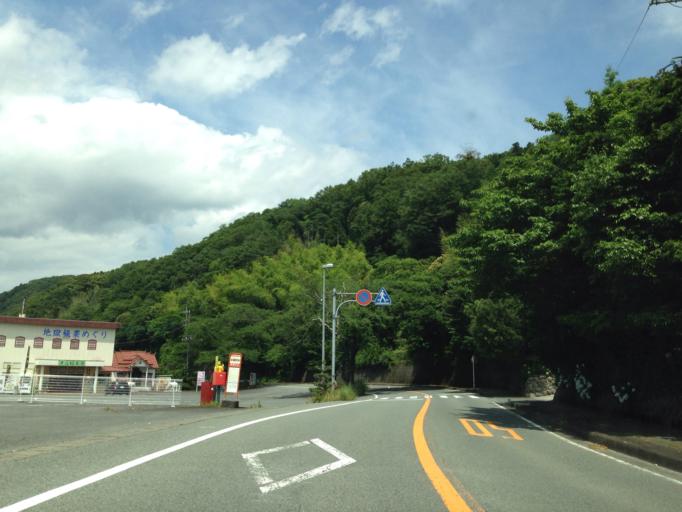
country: JP
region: Shizuoka
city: Heda
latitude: 34.9236
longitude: 138.9228
